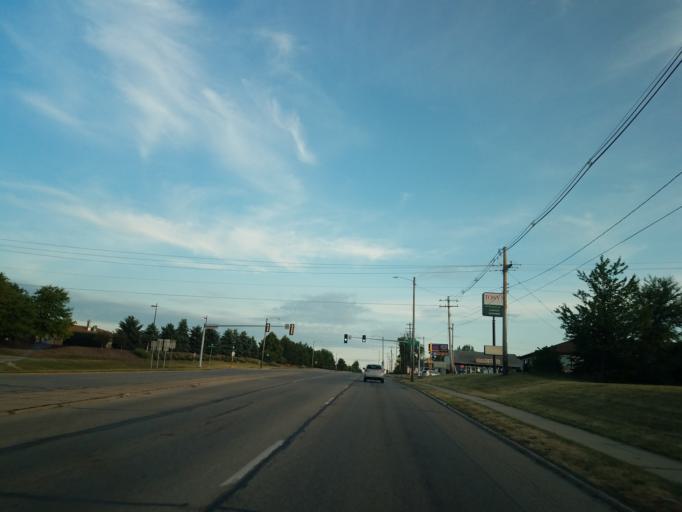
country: US
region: Illinois
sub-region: McLean County
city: Bloomington
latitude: 40.4576
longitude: -88.9929
